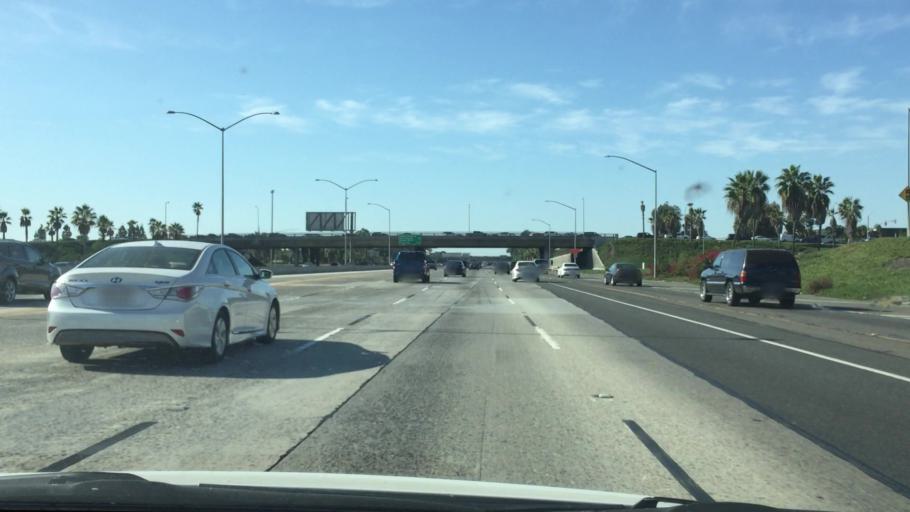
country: US
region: California
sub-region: Orange County
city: Costa Mesa
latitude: 33.6876
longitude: -117.8831
